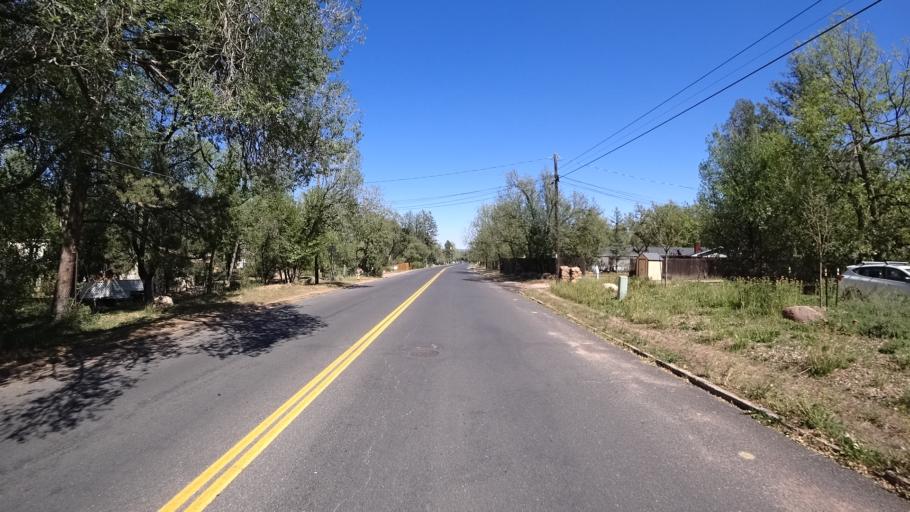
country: US
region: Colorado
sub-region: El Paso County
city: Colorado Springs
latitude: 38.8001
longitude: -104.8450
